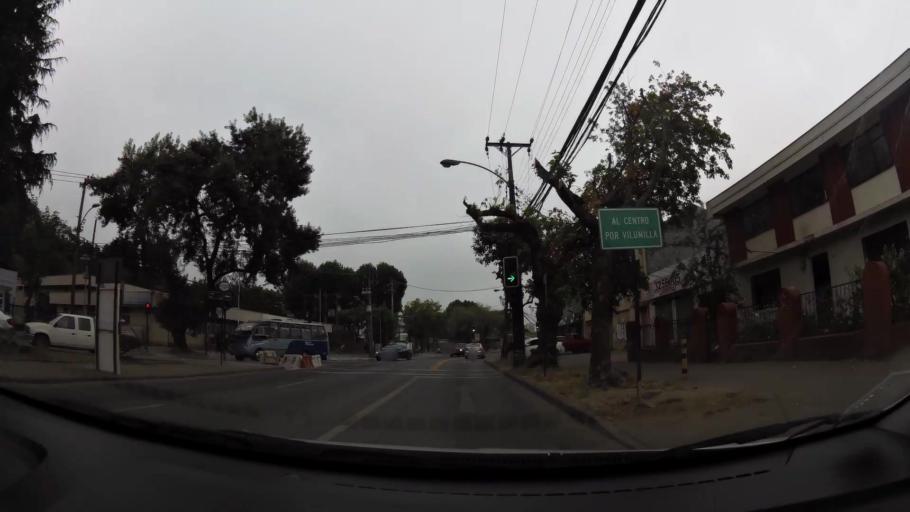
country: CL
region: Biobio
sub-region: Provincia de Concepcion
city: Concepcion
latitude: -36.8161
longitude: -73.0322
